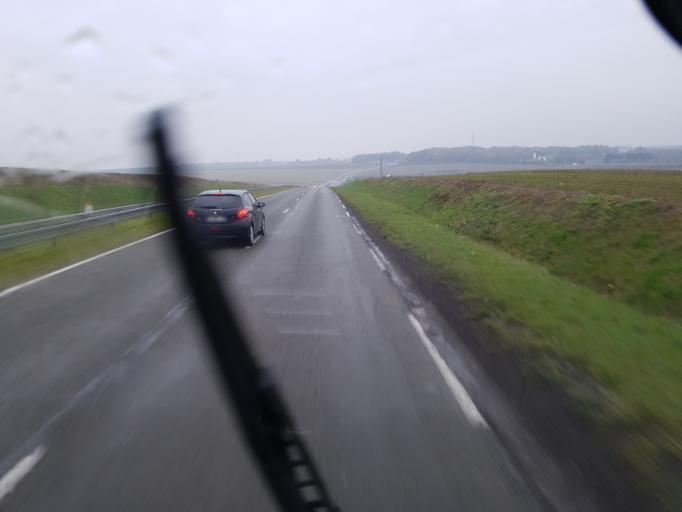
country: FR
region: Picardie
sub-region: Departement de l'Aisne
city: Essigny-le-Grand
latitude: 49.8037
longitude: 3.2860
